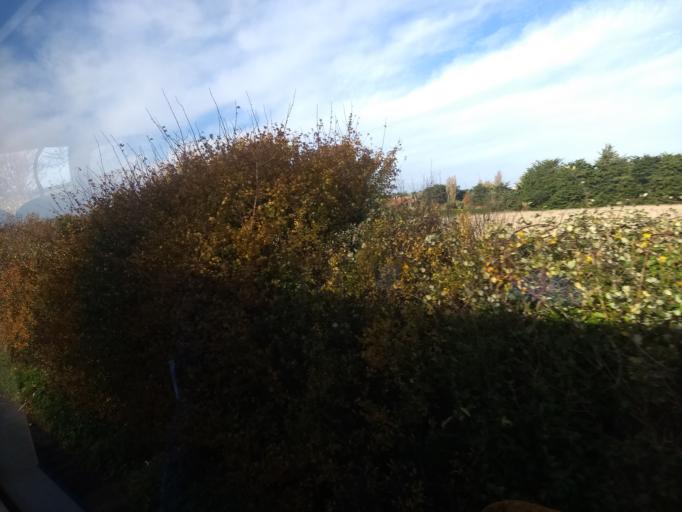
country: GB
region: England
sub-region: Isle of Wight
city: Yarmouth
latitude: 50.6979
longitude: -1.4783
